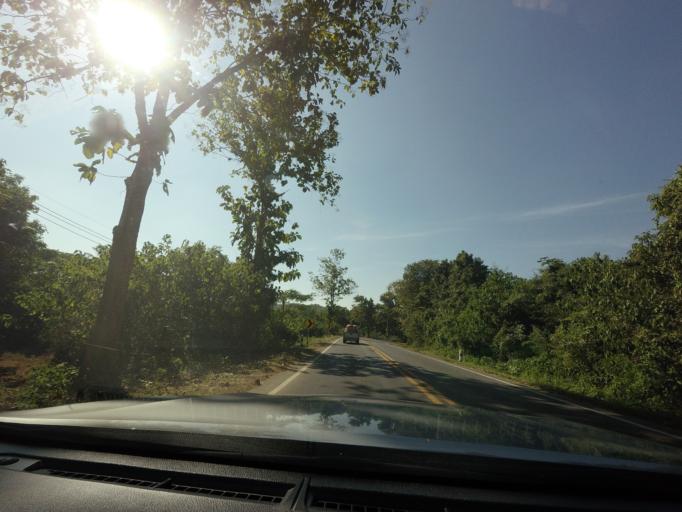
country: TH
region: Sukhothai
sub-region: Amphoe Si Satchanalai
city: Si Satchanalai
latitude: 17.6062
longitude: 99.7118
